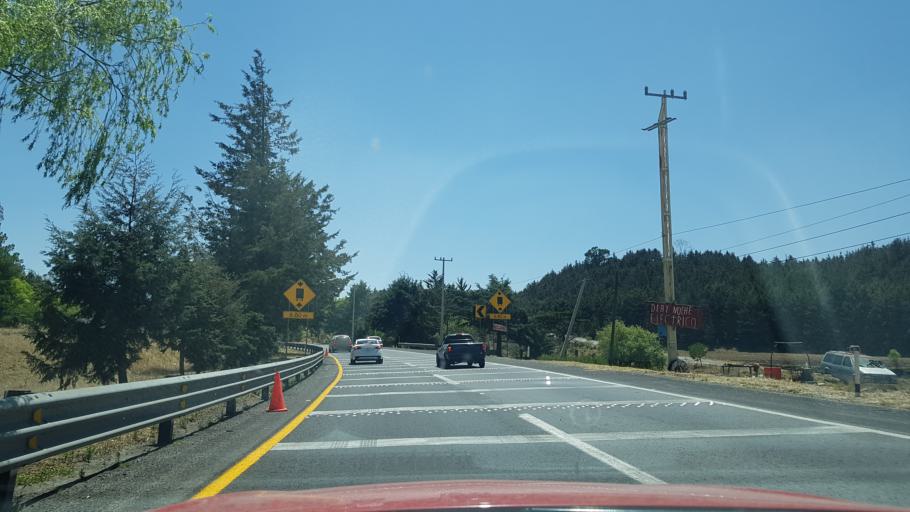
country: MX
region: Mexico
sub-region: Ixtlahuaca
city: San Lorenzo Toxico
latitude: 19.5281
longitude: -99.7454
